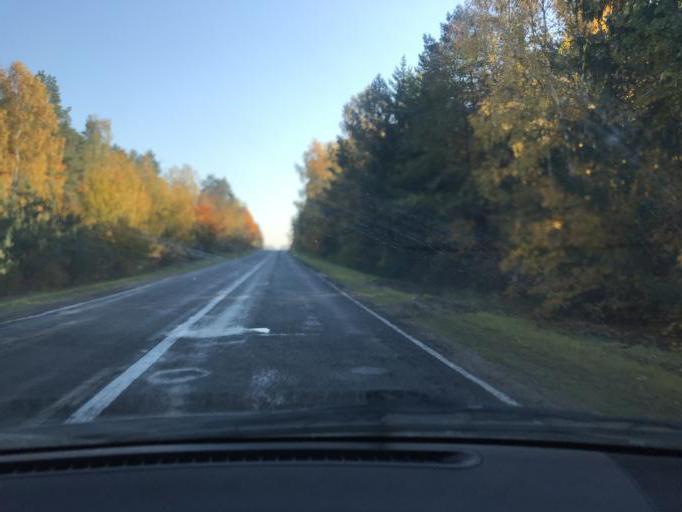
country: BY
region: Brest
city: Lyakhavichy
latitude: 52.9533
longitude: 26.2312
